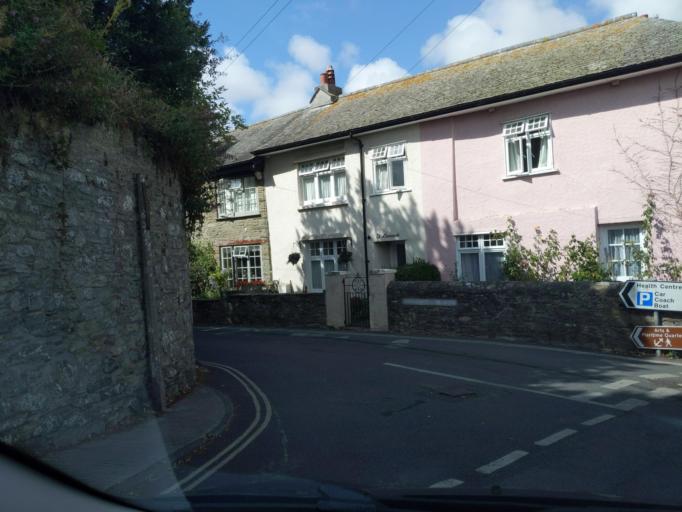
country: GB
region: England
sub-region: Devon
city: Salcombe
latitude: 50.2387
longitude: -3.7688
